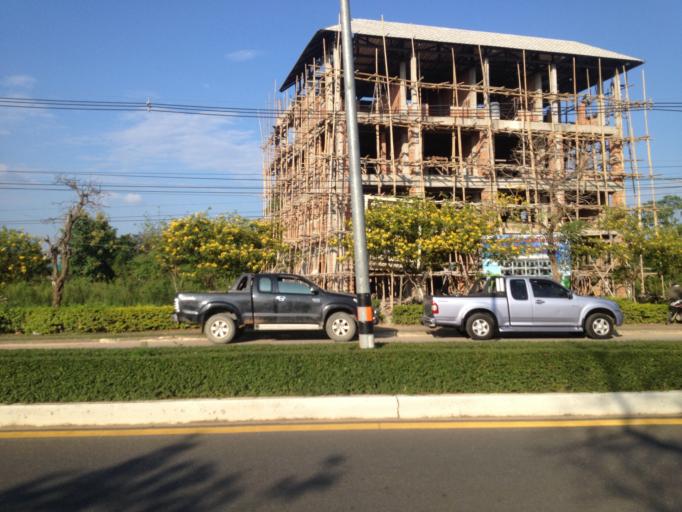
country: TH
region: Chiang Mai
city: Hang Dong
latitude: 18.7315
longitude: 98.9409
